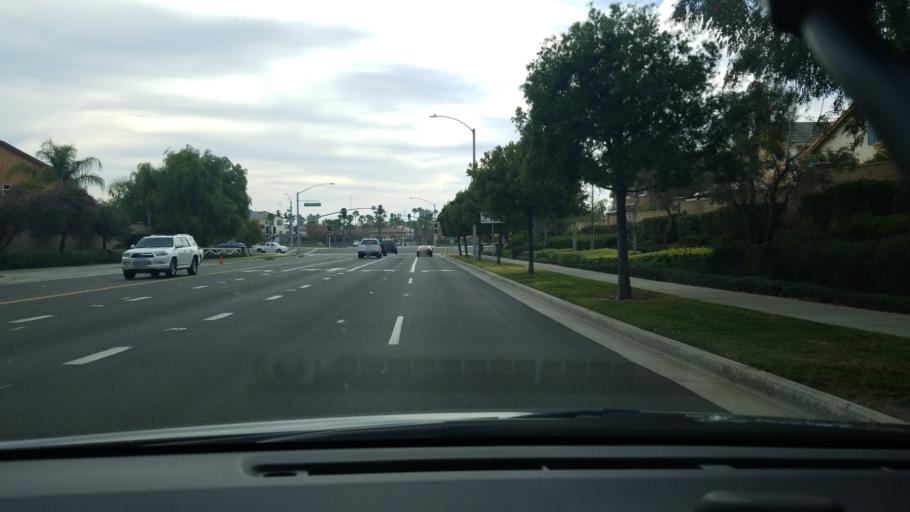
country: US
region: California
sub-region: Riverside County
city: Murrieta Hot Springs
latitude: 33.5555
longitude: -117.1110
